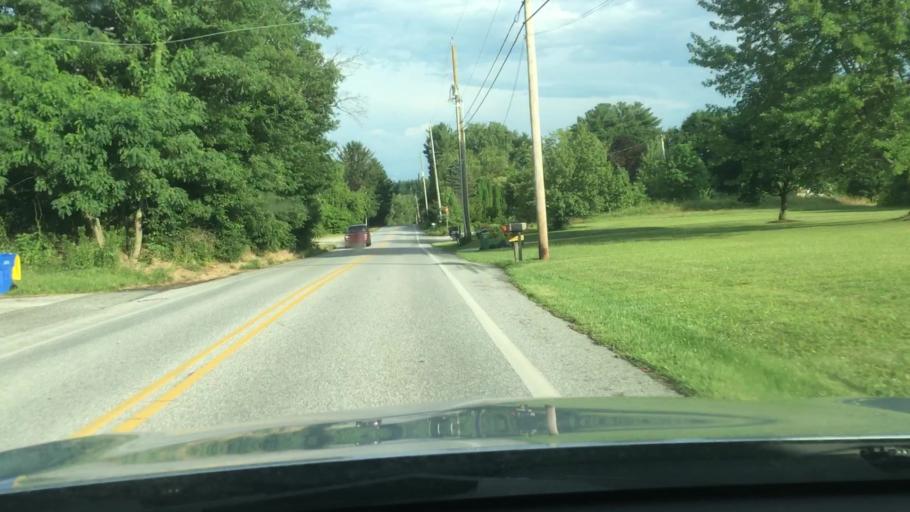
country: US
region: Pennsylvania
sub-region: York County
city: Weigelstown
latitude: 40.0138
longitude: -76.8099
